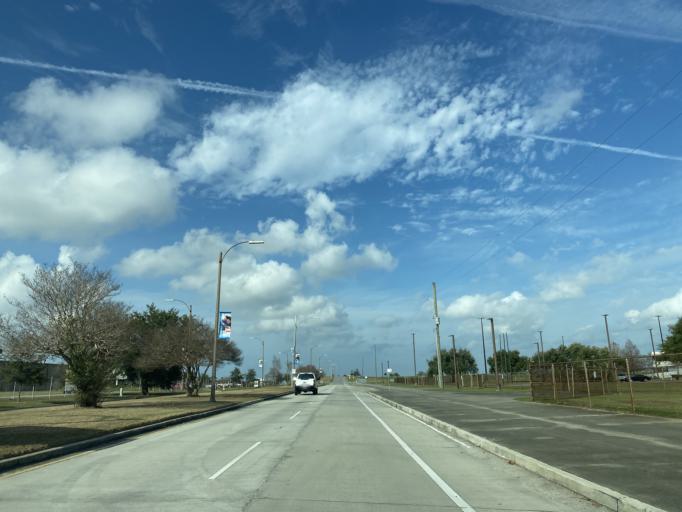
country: US
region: Louisiana
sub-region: Orleans Parish
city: New Orleans
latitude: 30.0290
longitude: -90.0523
